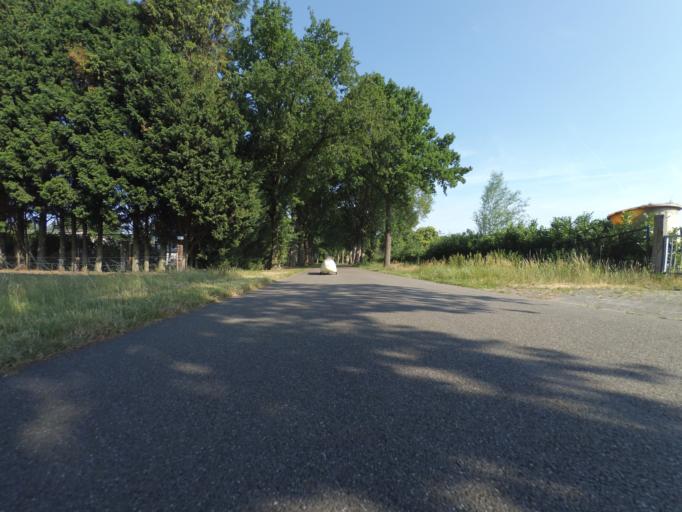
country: NL
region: North Brabant
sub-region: Gemeente Woensdrecht
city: Woensdrecht
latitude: 51.4372
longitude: 4.3733
